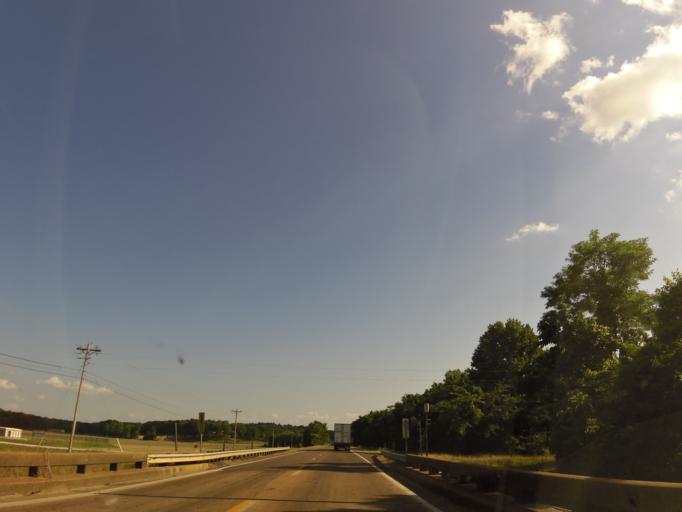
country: US
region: Mississippi
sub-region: Lafayette County
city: University
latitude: 34.2730
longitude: -89.5215
